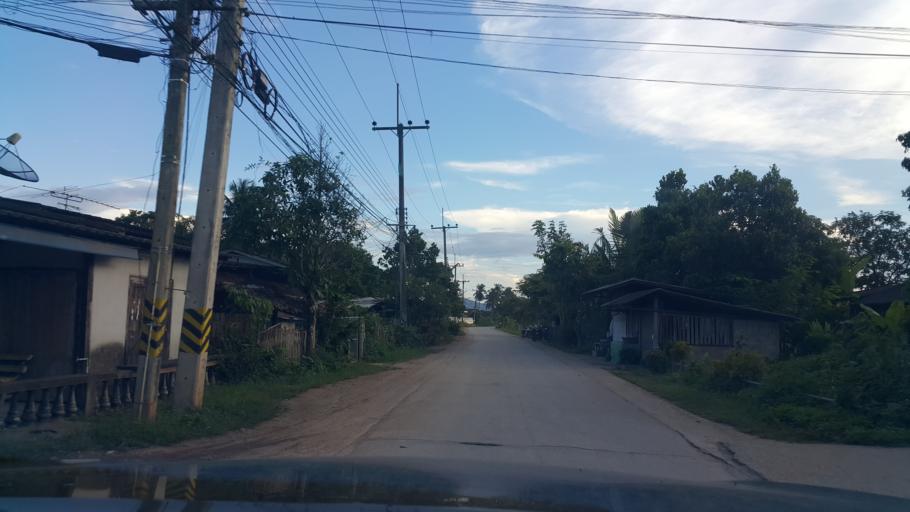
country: TH
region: Chiang Mai
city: Mae Taeng
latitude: 19.1571
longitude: 99.0092
